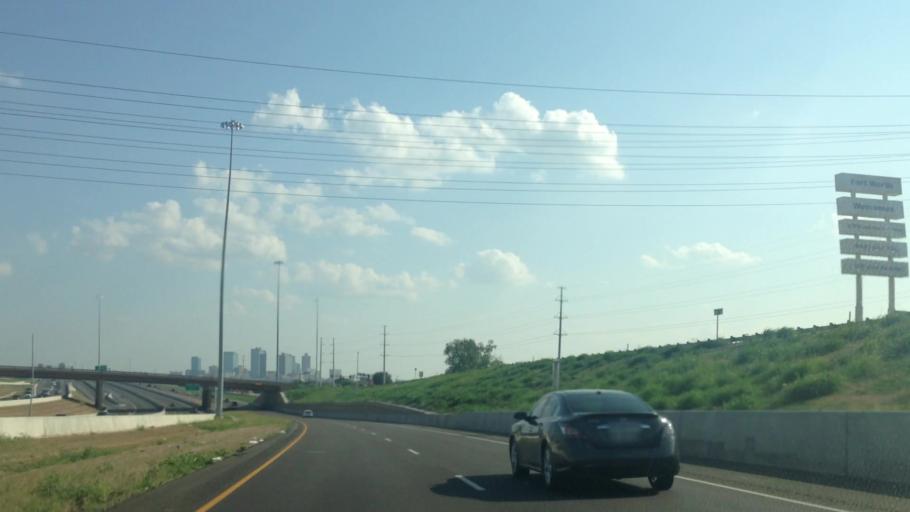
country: US
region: Texas
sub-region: Tarrant County
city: Haltom City
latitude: 32.7984
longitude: -97.3217
